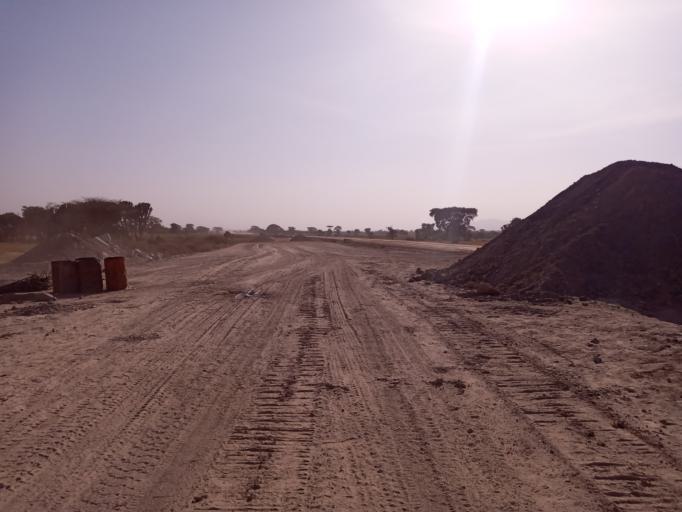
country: ET
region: Oromiya
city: Shashemene
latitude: 7.3055
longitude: 38.6193
